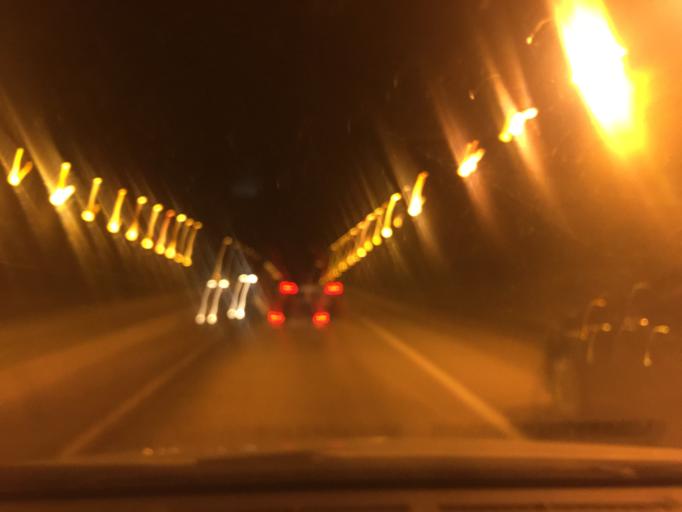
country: JO
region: Amman
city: Amman
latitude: 31.9490
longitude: 35.8925
